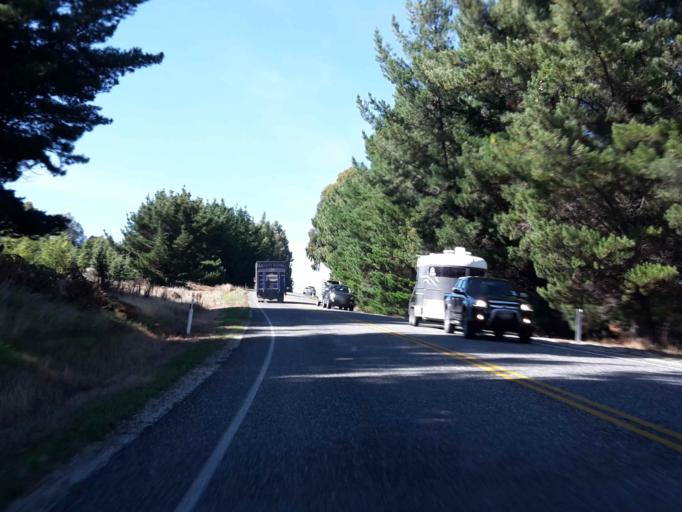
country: NZ
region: Otago
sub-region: Queenstown-Lakes District
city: Wanaka
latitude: -44.7054
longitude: 169.1981
